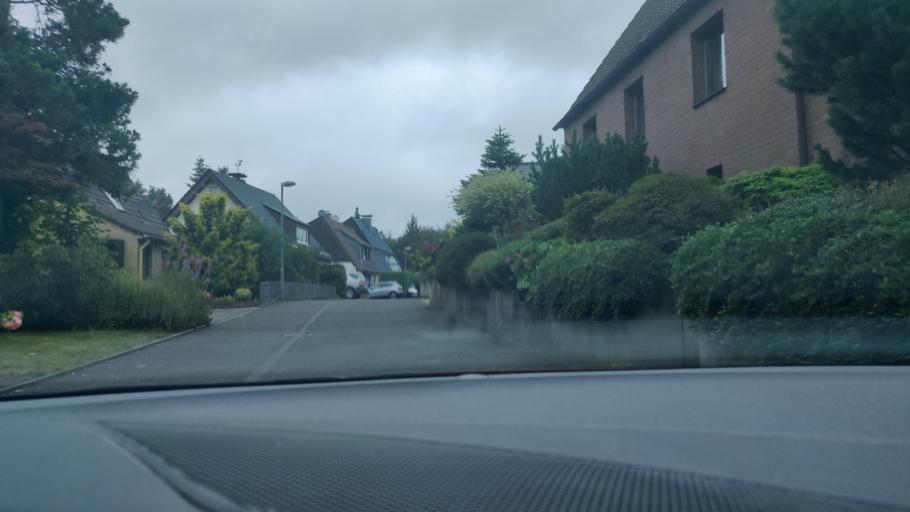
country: DE
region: North Rhine-Westphalia
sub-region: Regierungsbezirk Dusseldorf
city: Velbert
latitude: 51.3544
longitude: 7.0311
